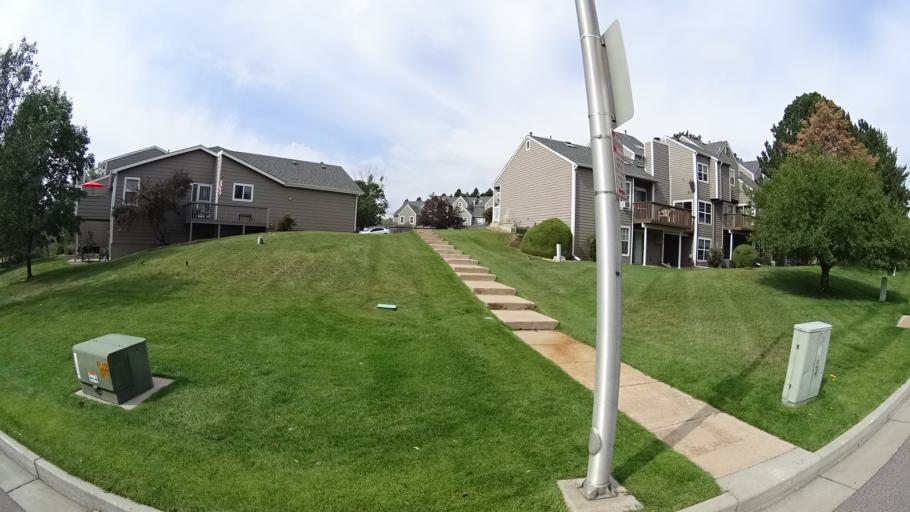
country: US
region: Colorado
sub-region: El Paso County
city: Colorado Springs
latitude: 38.8925
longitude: -104.7866
